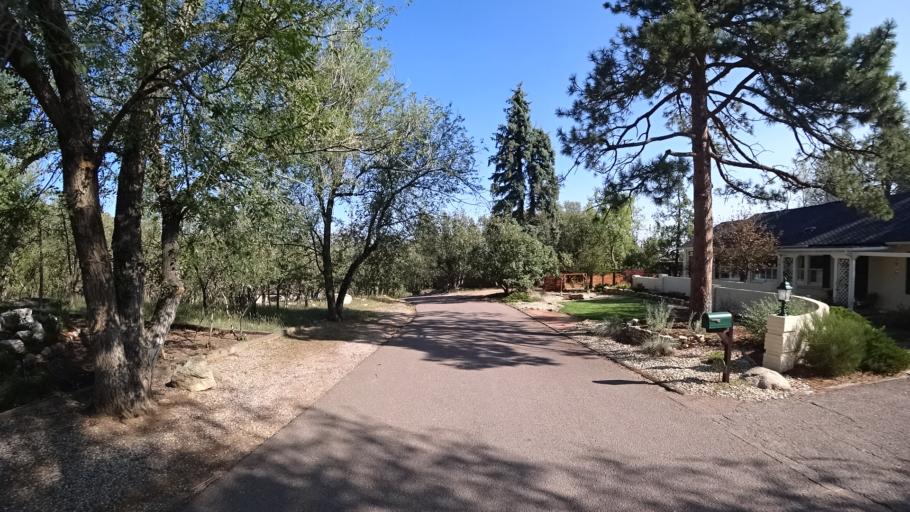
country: US
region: Colorado
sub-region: El Paso County
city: Colorado Springs
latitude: 38.7963
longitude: -104.8507
